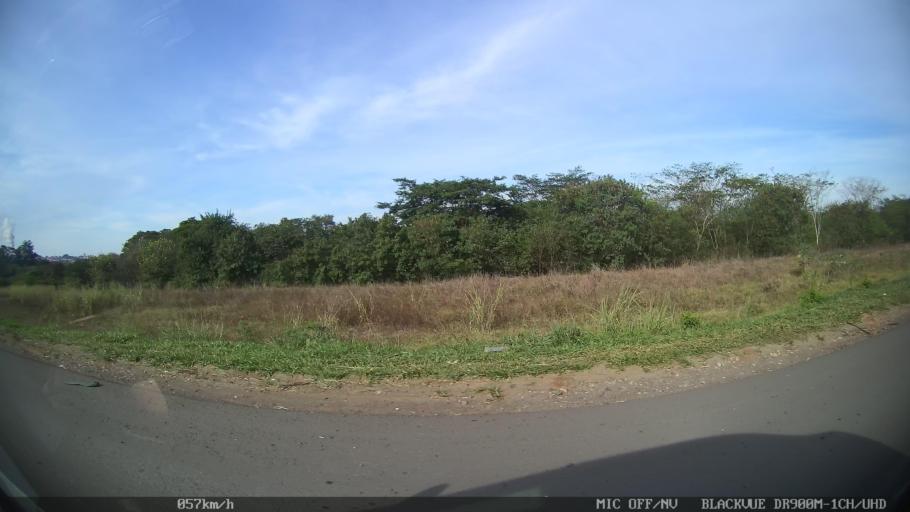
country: BR
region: Sao Paulo
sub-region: Piracicaba
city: Piracicaba
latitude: -22.6844
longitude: -47.6819
